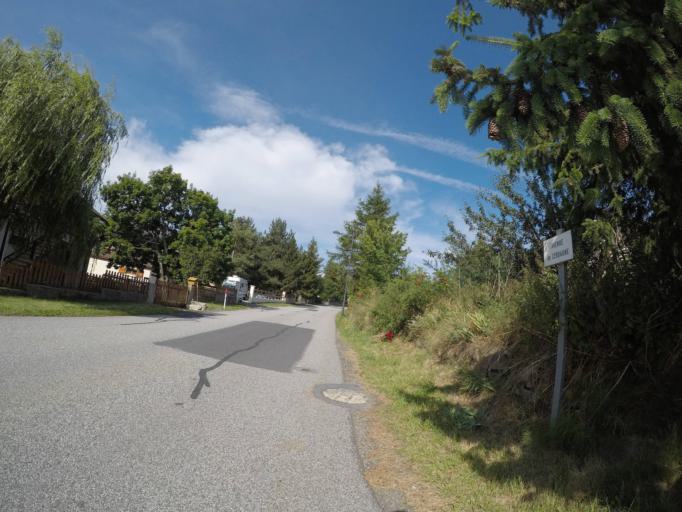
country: ES
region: Catalonia
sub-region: Provincia de Girona
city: Llivia
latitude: 42.5008
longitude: 2.1062
